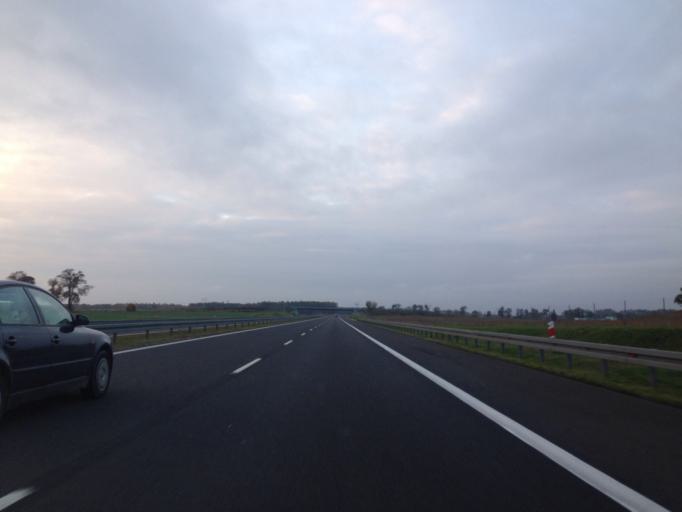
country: PL
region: Kujawsko-Pomorskie
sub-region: Powiat swiecki
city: Warlubie
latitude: 53.5613
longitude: 18.6099
